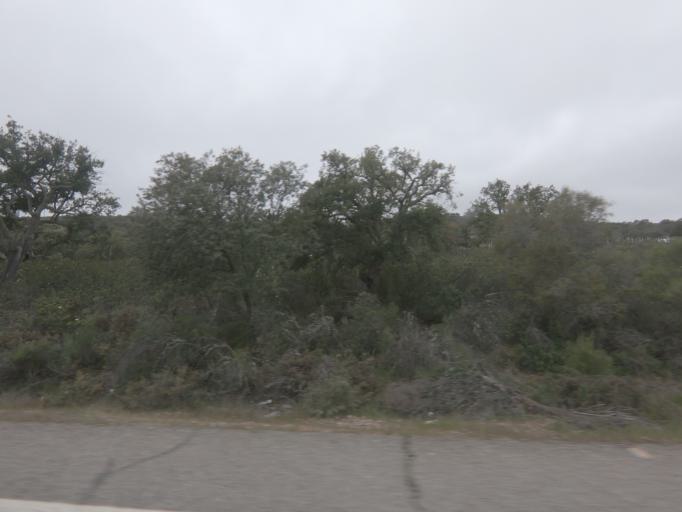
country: ES
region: Extremadura
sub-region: Provincia de Badajoz
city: Puebla de Obando
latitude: 39.2787
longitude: -6.5207
